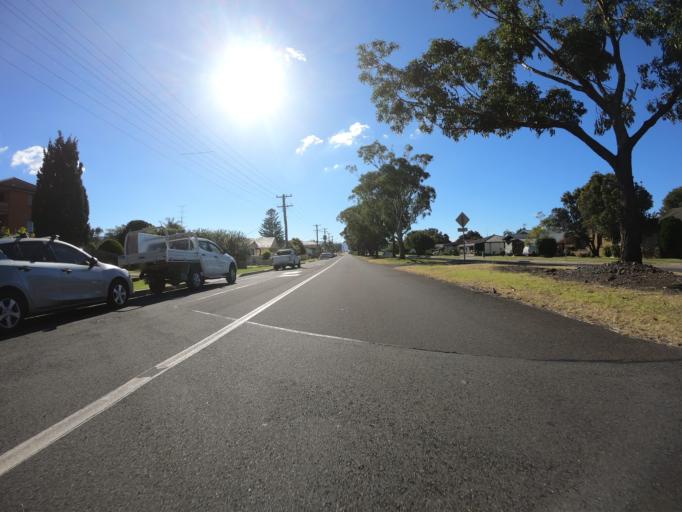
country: AU
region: New South Wales
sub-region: Wollongong
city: East Corrimal
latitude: -34.3704
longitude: 150.9160
